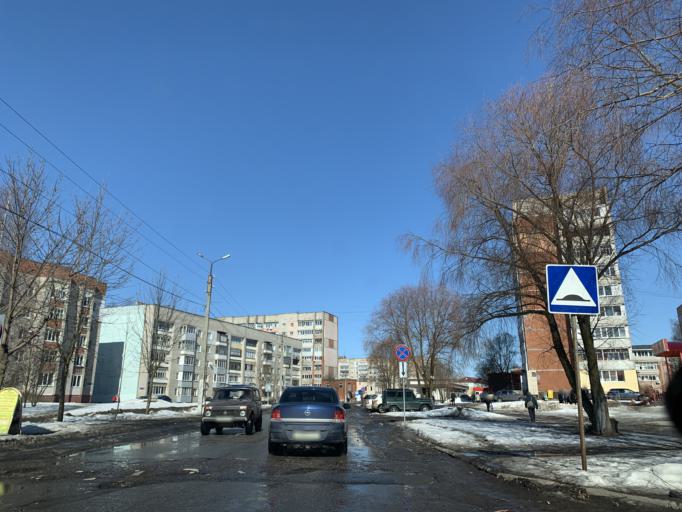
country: RU
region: Jaroslavl
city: Tutayev
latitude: 57.8621
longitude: 39.5109
